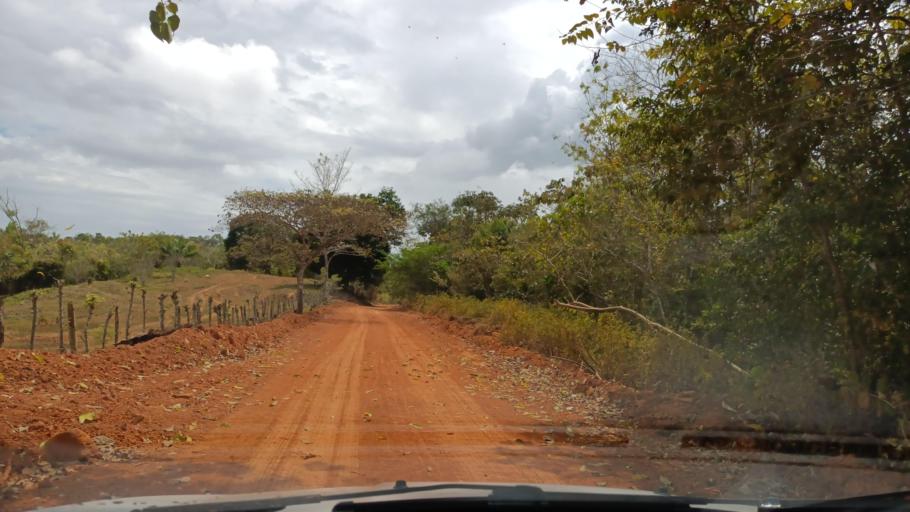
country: PA
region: Panama
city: La Cabima
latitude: 9.1289
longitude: -79.4982
